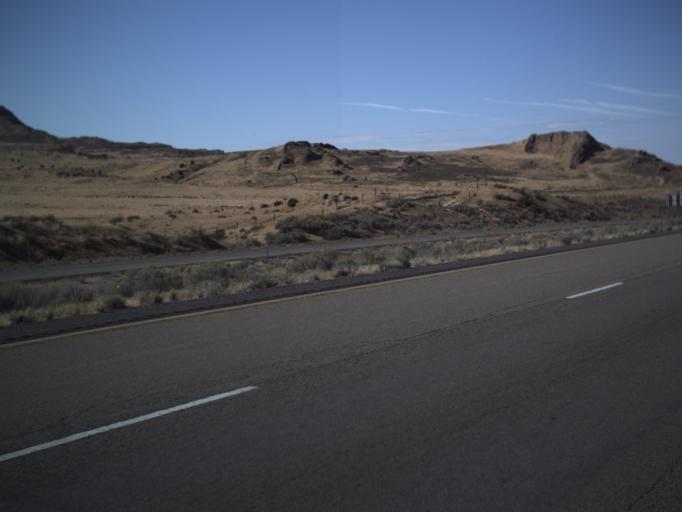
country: US
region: Utah
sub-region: Tooele County
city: Grantsville
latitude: 40.8203
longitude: -112.9075
